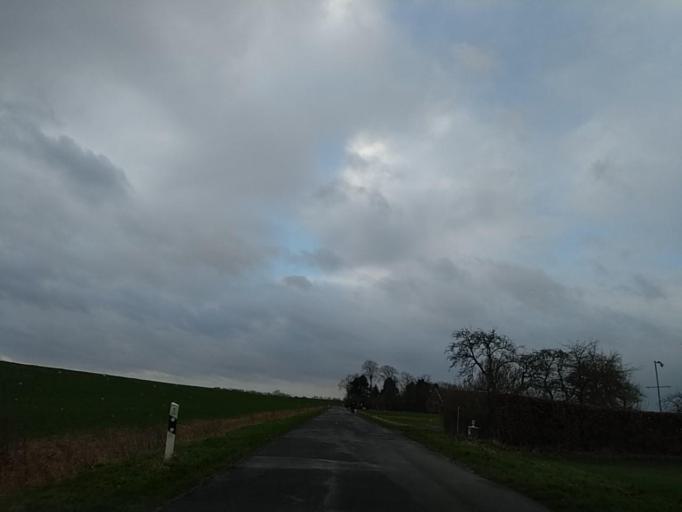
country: DE
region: Lower Saxony
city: Bunde
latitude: 53.2308
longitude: 7.2252
